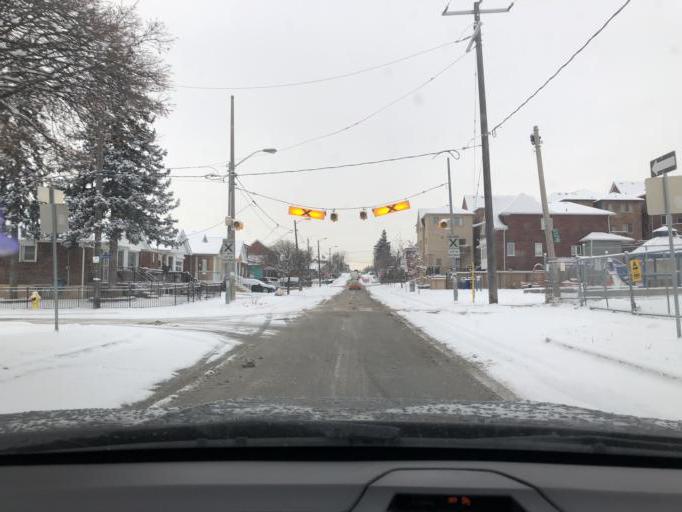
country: CA
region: Ontario
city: Toronto
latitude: 43.6870
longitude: -79.4711
